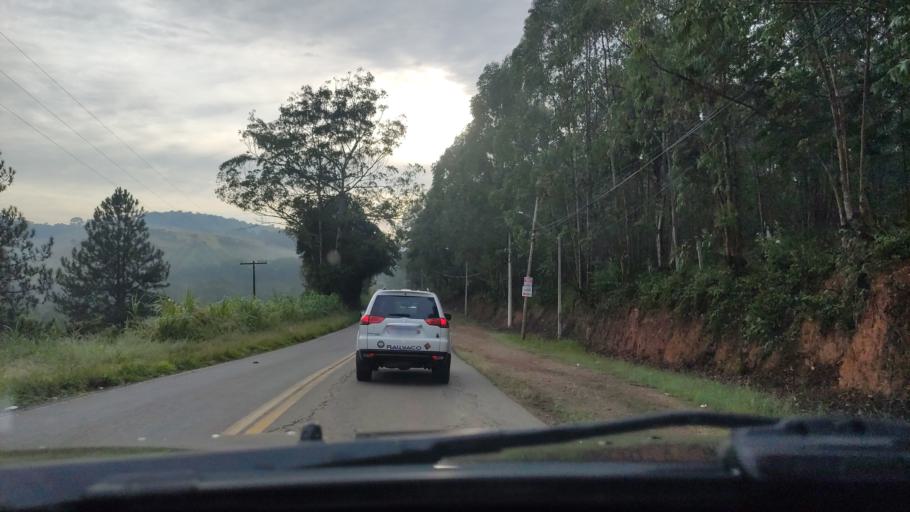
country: BR
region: Sao Paulo
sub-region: Jarinu
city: Jarinu
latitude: -23.1220
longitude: -46.7700
